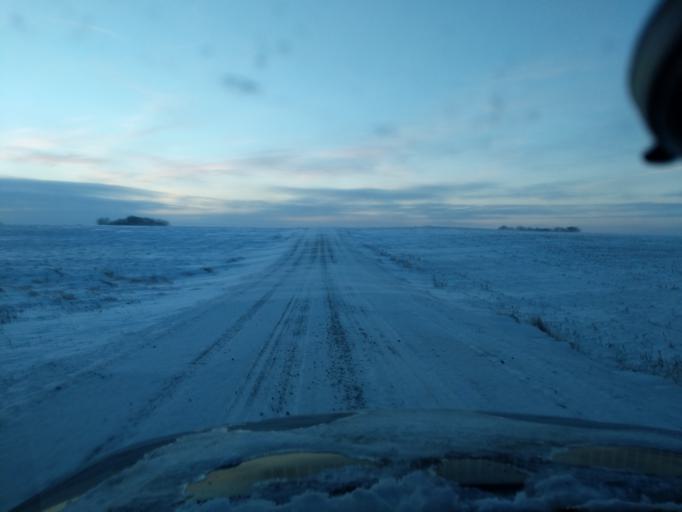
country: US
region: Minnesota
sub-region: Renville County
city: Renville
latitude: 44.7271
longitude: -95.3437
